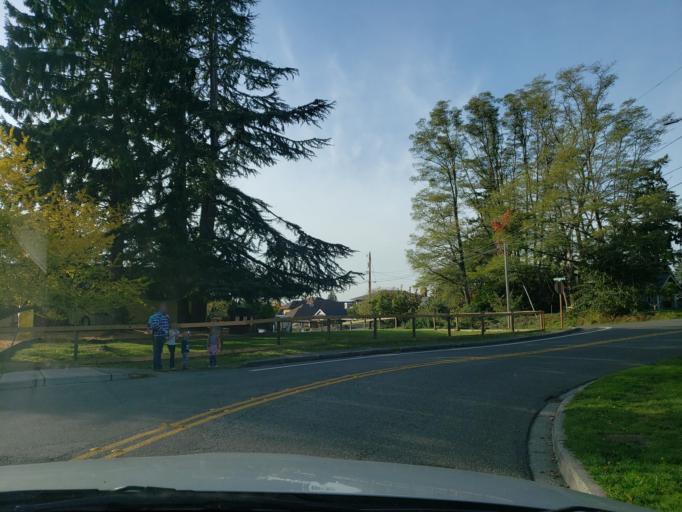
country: US
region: Washington
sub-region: Snohomish County
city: Mukilteo
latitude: 47.9348
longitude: -122.3010
